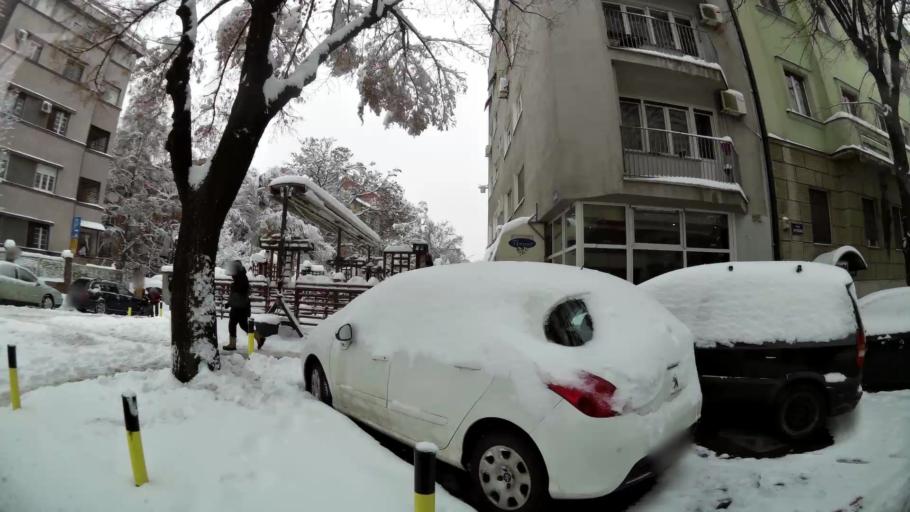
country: RS
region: Central Serbia
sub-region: Belgrade
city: Vracar
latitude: 44.8002
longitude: 20.4745
